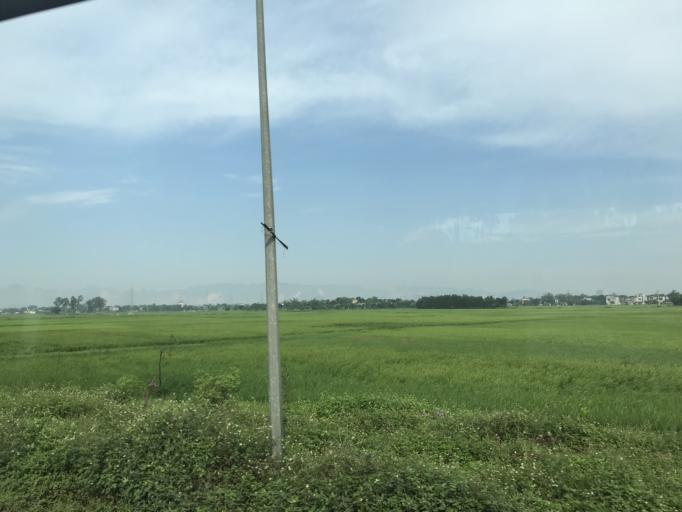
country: VN
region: Ha Nam
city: Thanh Pho Phu Ly
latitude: 20.5166
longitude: 105.9424
